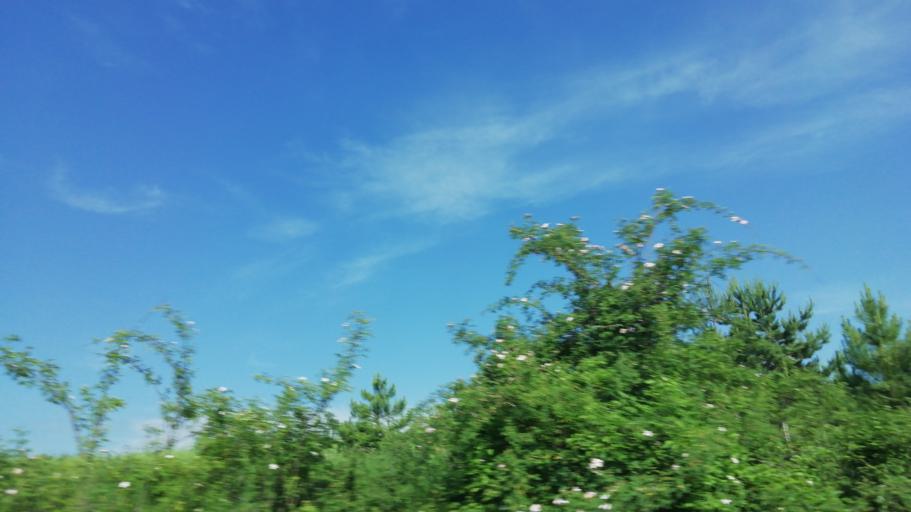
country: TR
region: Karabuk
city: Karabuk
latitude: 41.0894
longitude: 32.5875
